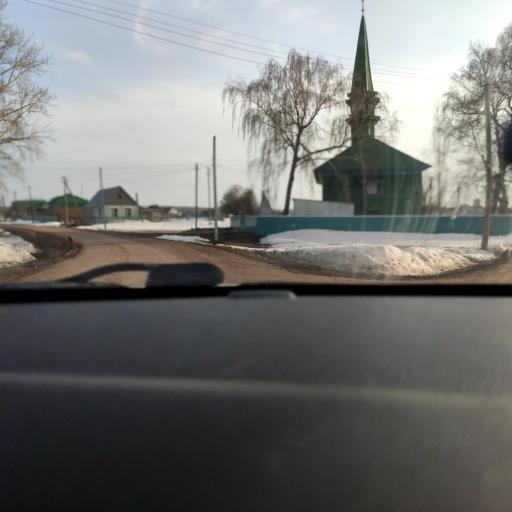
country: RU
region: Bashkortostan
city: Avdon
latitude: 54.4809
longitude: 55.5929
